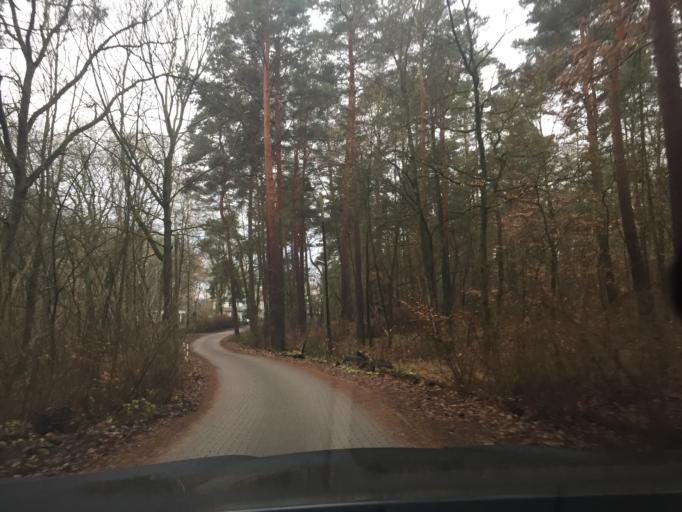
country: DE
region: Berlin
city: Kladow
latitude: 52.4538
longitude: 13.1074
